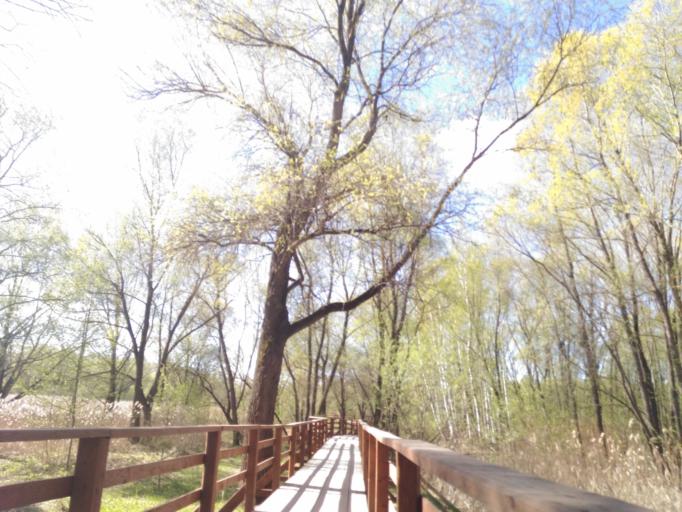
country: RU
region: Moscow
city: Shchukino
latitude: 55.7789
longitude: 37.4305
